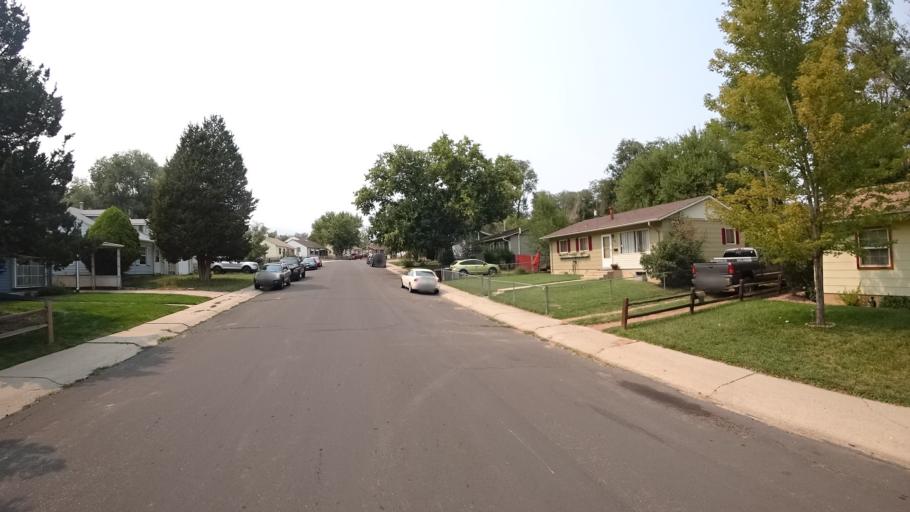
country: US
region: Colorado
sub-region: El Paso County
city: Colorado Springs
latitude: 38.7987
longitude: -104.8151
